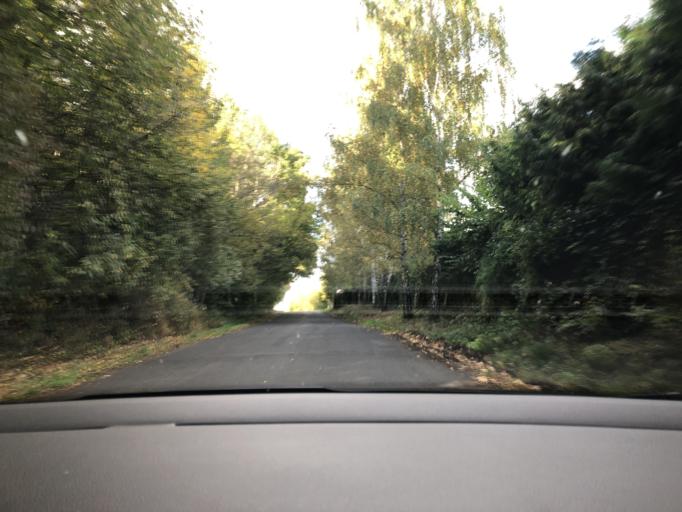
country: CZ
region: Ustecky
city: Zitenice
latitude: 50.5903
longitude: 14.1650
